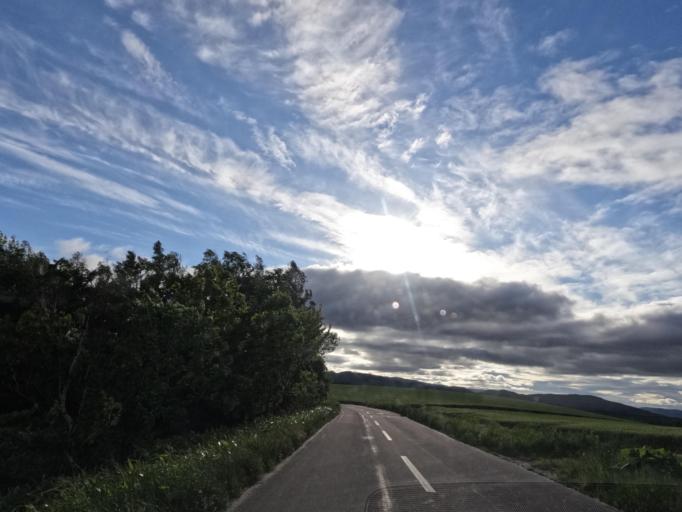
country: JP
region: Hokkaido
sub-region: Asahikawa-shi
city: Asahikawa
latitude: 43.6243
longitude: 142.4425
